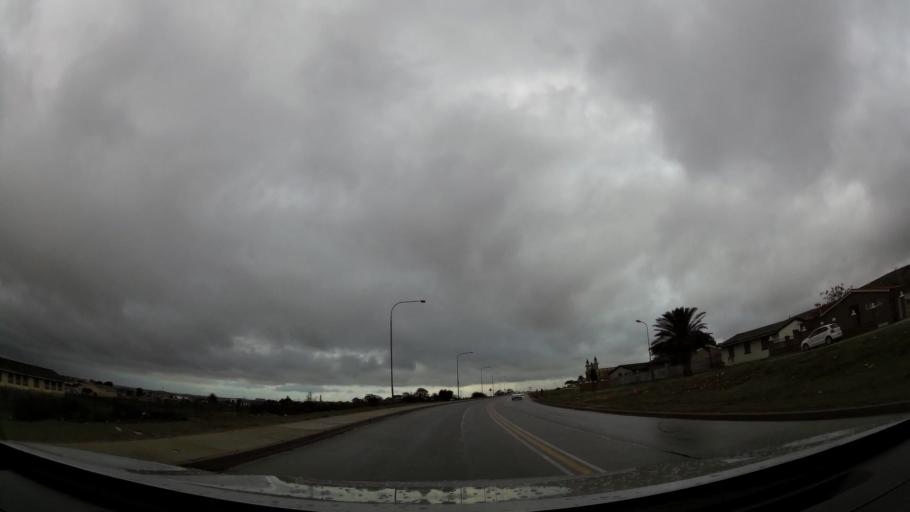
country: ZA
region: Eastern Cape
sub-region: Nelson Mandela Bay Metropolitan Municipality
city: Port Elizabeth
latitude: -33.8871
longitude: 25.5148
